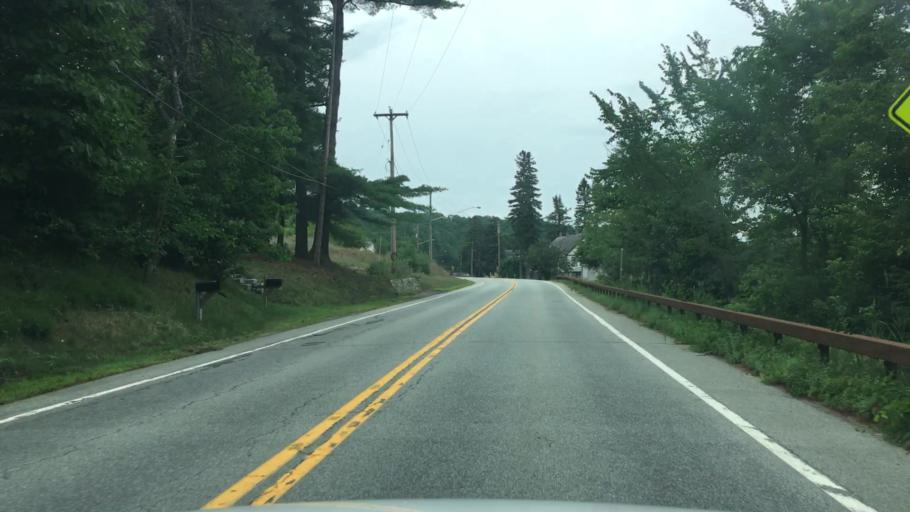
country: US
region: New York
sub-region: Clinton County
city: Peru
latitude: 44.4304
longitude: -73.6802
